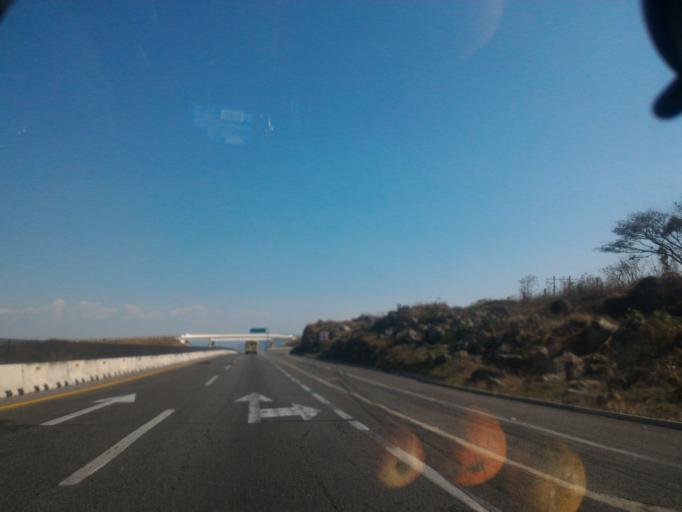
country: MX
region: Jalisco
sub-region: Zapotlan el Grande
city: Ciudad Guzman [CERESO]
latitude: 19.6447
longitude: -103.4727
